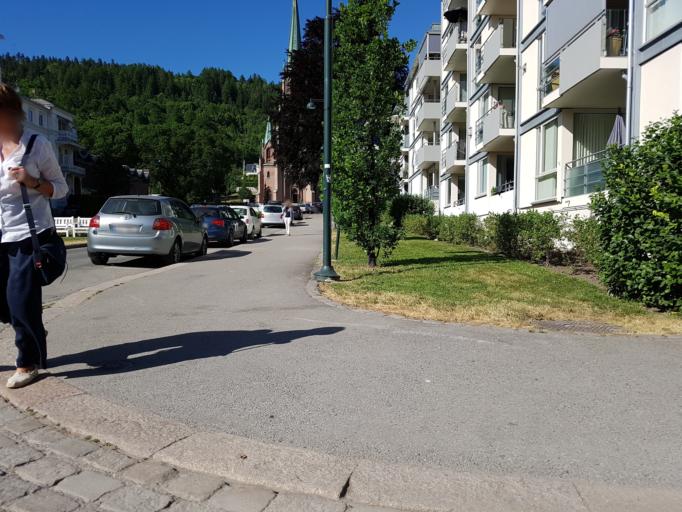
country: NO
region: Buskerud
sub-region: Drammen
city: Drammen
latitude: 59.7451
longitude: 10.2056
